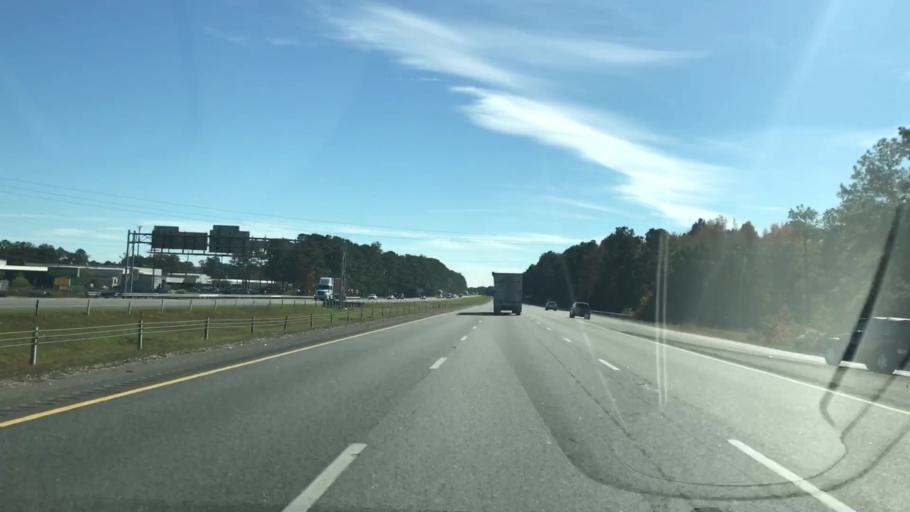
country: US
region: South Carolina
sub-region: Berkeley County
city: Sangaree
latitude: 33.0364
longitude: -80.1470
